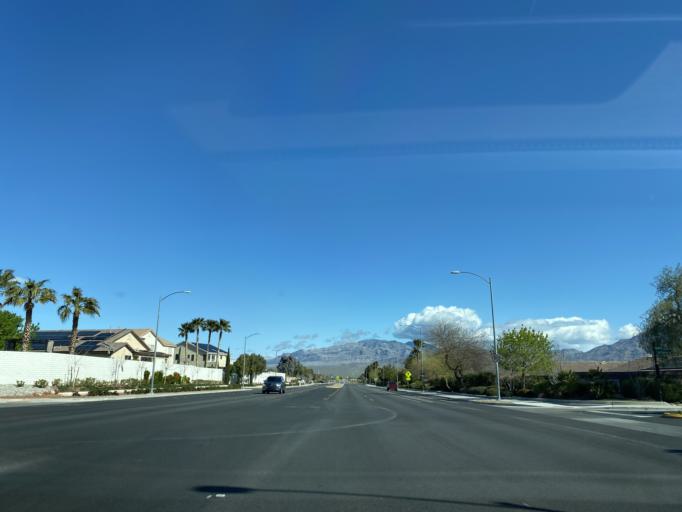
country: US
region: Nevada
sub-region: Clark County
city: Las Vegas
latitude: 36.3117
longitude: -115.2786
